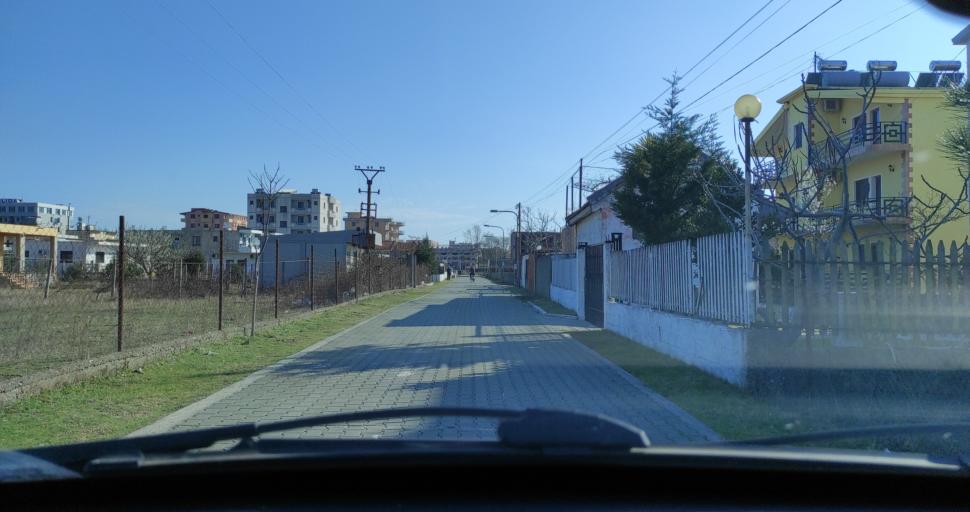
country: AL
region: Shkoder
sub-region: Rrethi i Shkodres
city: Velipoje
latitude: 41.8685
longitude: 19.4212
